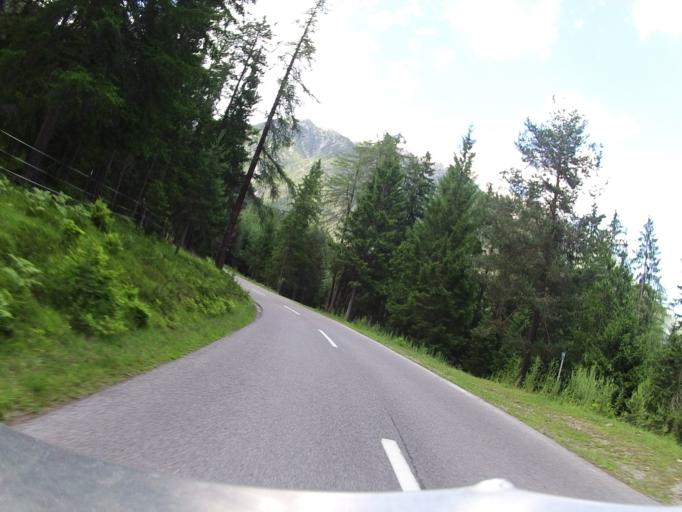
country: AT
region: Tyrol
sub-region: Politischer Bezirk Imst
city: Tarrenz
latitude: 47.2739
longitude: 10.7432
